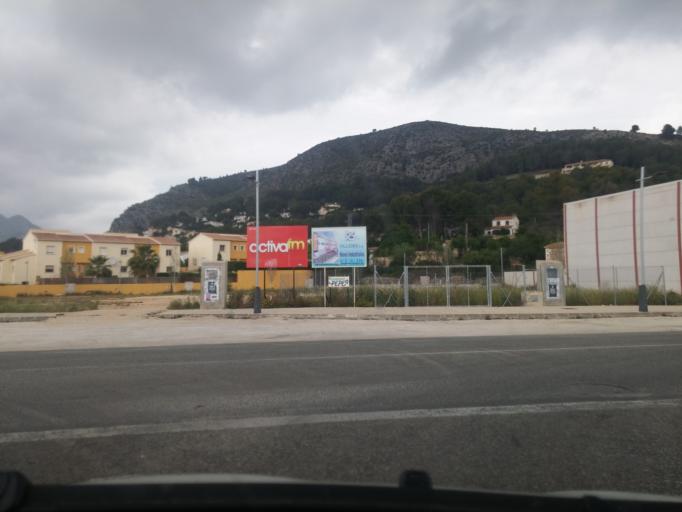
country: ES
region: Valencia
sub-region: Provincia de Alicante
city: Alcalali
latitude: 38.7520
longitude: -0.0417
